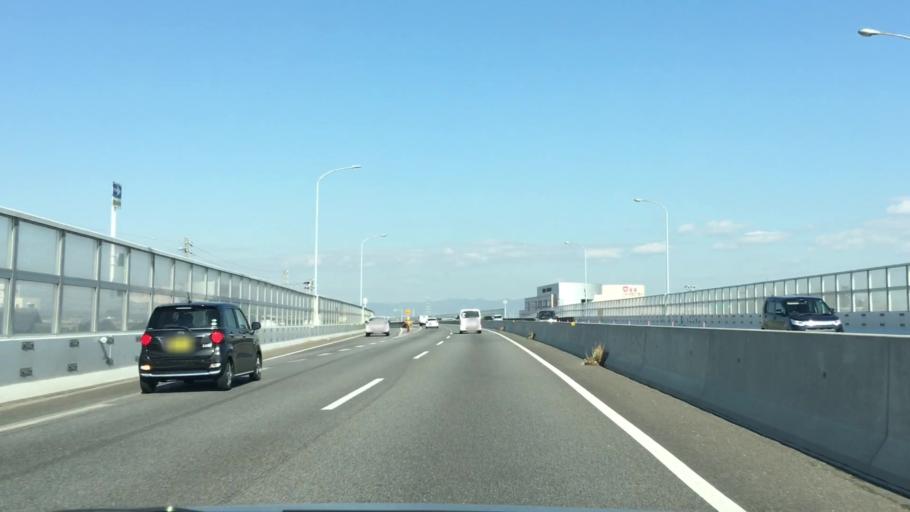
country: JP
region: Aichi
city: Toyohashi
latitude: 34.7240
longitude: 137.3545
